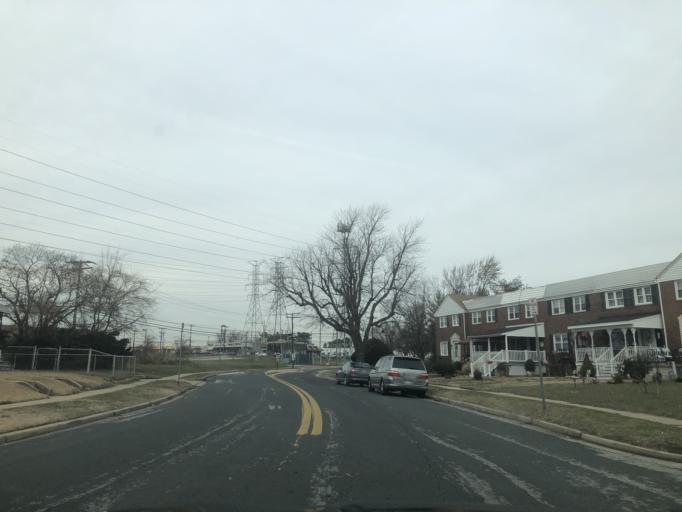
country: US
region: Maryland
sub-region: Baltimore County
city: Dundalk
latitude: 39.2669
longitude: -76.4994
